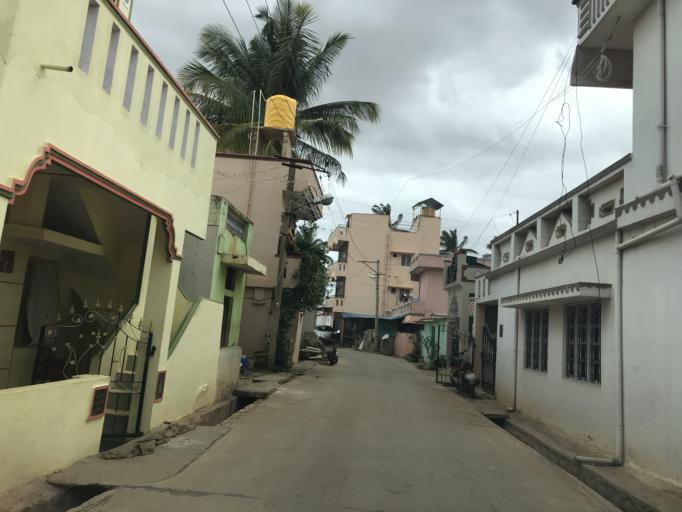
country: IN
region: Karnataka
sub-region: Bangalore Rural
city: Devanhalli
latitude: 13.2164
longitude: 77.6565
